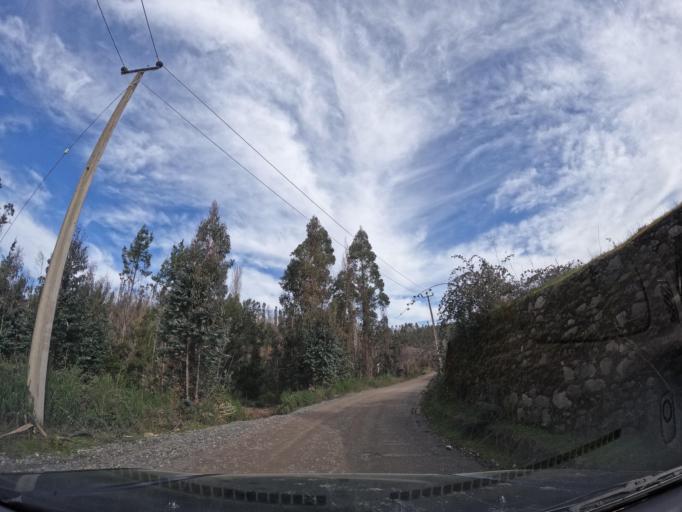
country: CL
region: Biobio
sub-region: Provincia de Concepcion
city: Chiguayante
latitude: -37.0136
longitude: -72.9091
